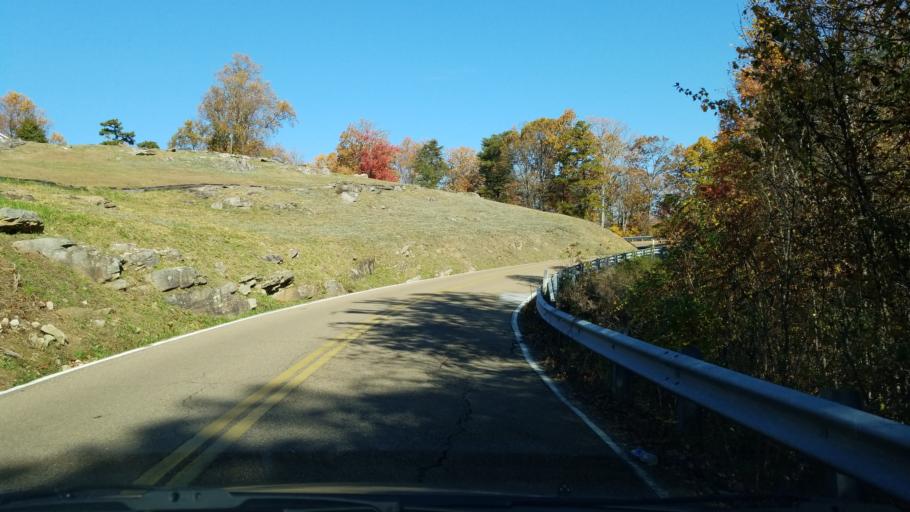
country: US
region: Tennessee
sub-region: Hamilton County
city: Soddy-Daisy
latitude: 35.2535
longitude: -85.1977
